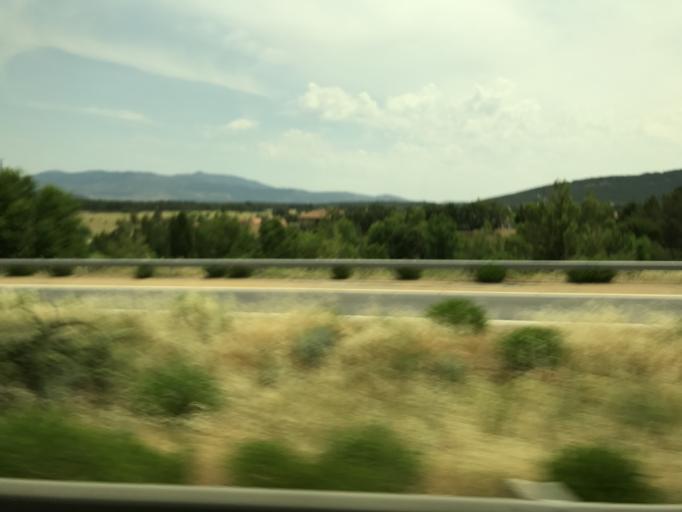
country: ES
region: Madrid
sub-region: Provincia de Madrid
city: Buitrago del Lozoya
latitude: 40.9779
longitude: -3.6384
